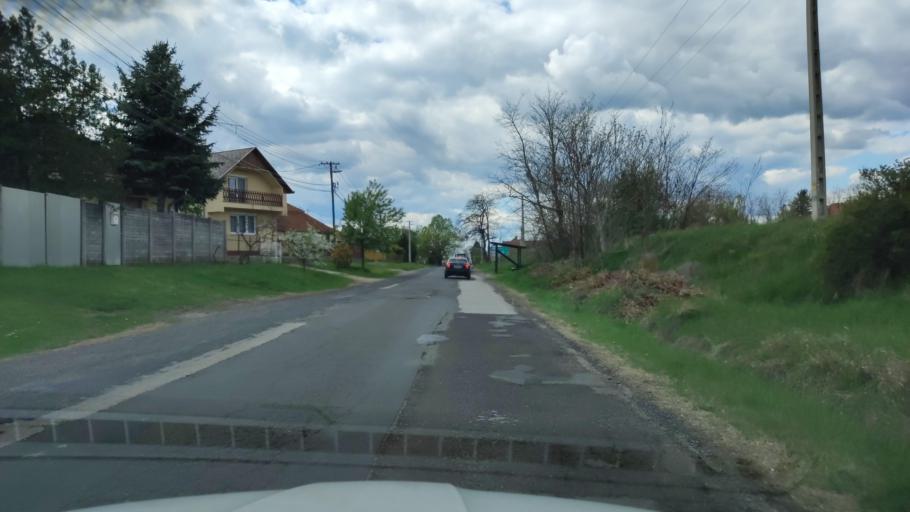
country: HU
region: Pest
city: Cegledbercel
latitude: 47.2170
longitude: 19.6876
